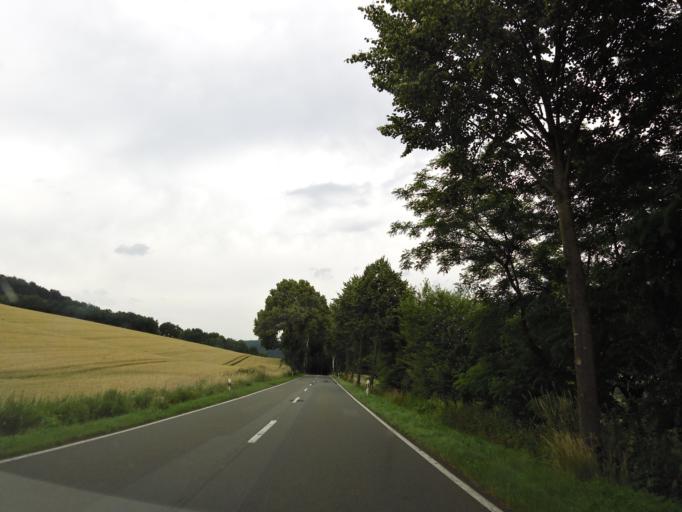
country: DE
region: Lower Saxony
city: Buhren
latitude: 51.5323
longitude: 9.6158
